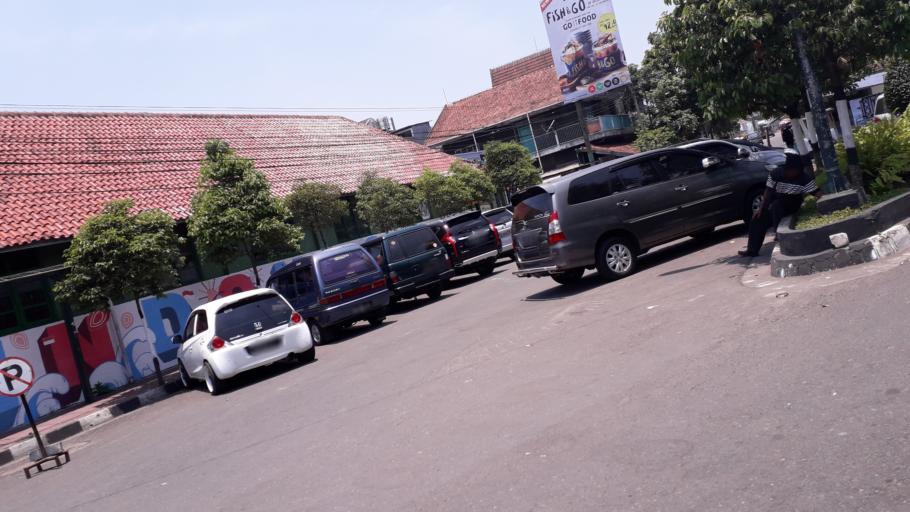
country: ID
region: Daerah Istimewa Yogyakarta
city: Yogyakarta
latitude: -7.7854
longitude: 110.3607
